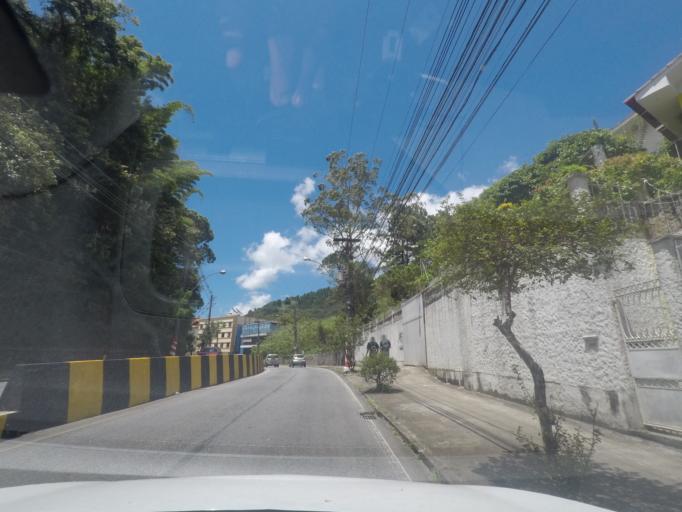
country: BR
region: Rio de Janeiro
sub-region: Teresopolis
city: Teresopolis
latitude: -22.4269
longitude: -42.9805
